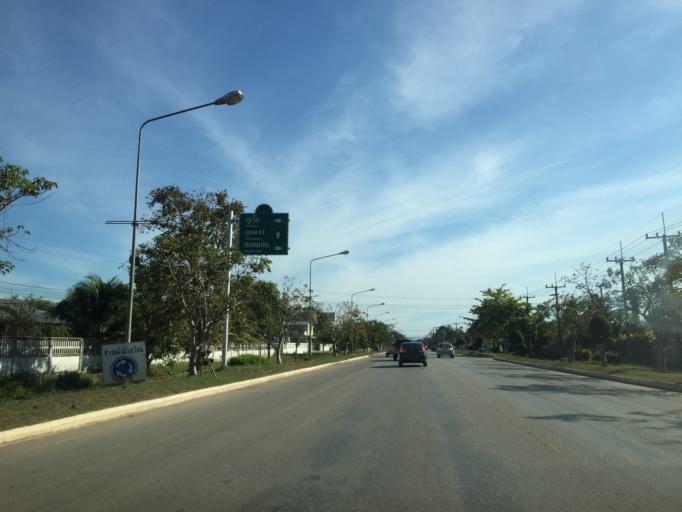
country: TH
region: Loei
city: Wang Saphung
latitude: 17.3170
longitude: 101.7624
